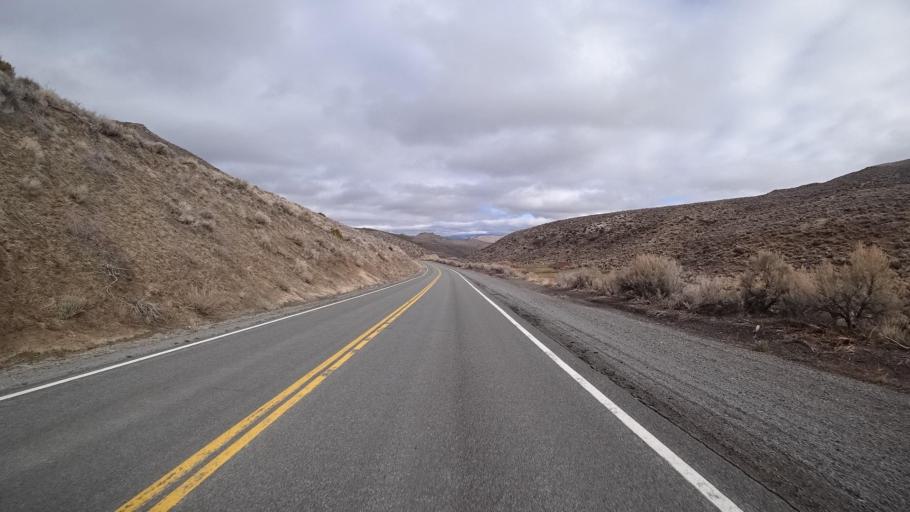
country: US
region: Nevada
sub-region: Washoe County
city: Cold Springs
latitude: 39.8139
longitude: -119.9340
